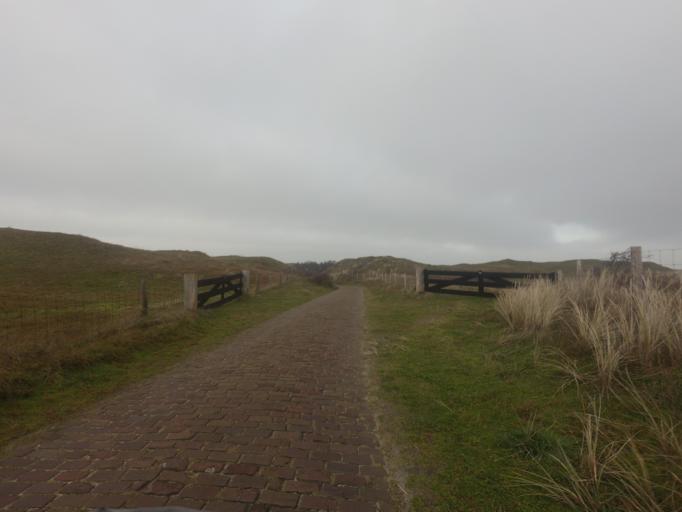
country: NL
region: North Holland
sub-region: Gemeente Texel
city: Den Burg
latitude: 53.1197
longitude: 4.8018
